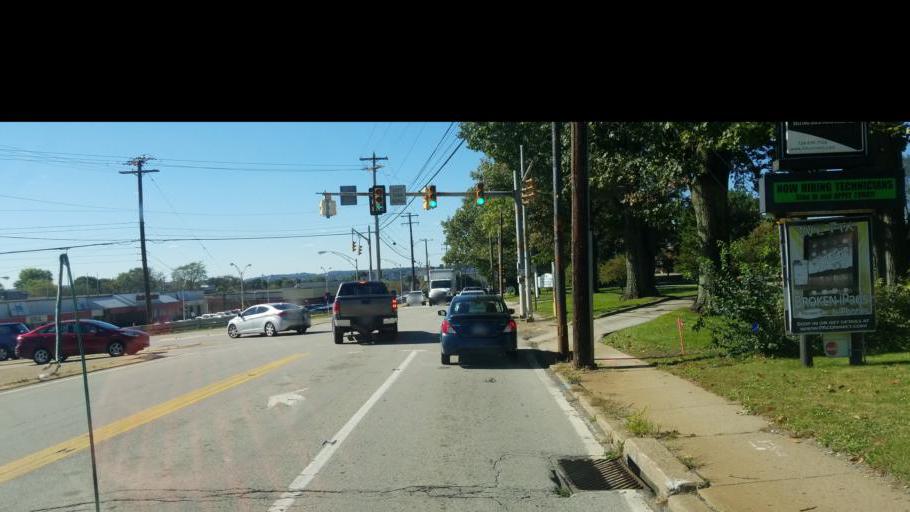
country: US
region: Pennsylvania
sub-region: Westmoreland County
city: Greensburg
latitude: 40.3023
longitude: -79.5251
